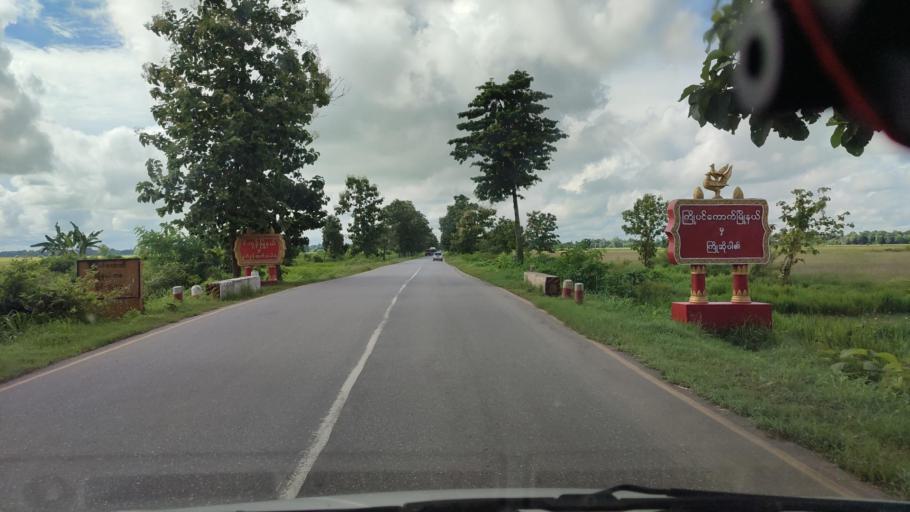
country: MM
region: Bago
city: Paungde
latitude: 18.2996
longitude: 95.6333
